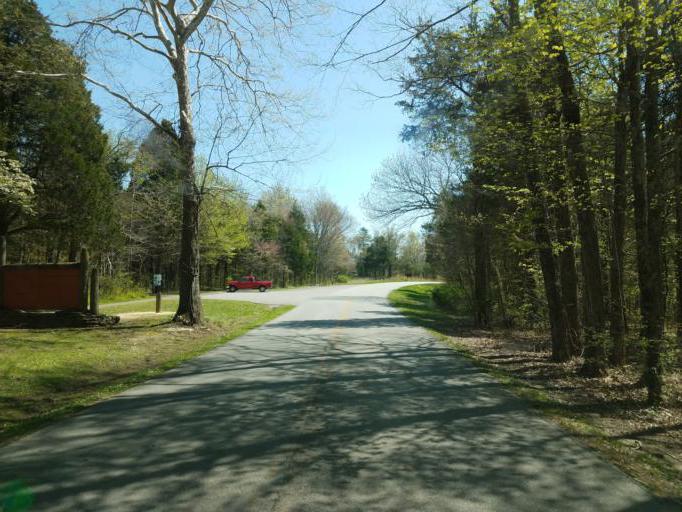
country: US
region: Kentucky
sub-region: Barren County
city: Cave City
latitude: 37.1527
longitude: -86.0486
